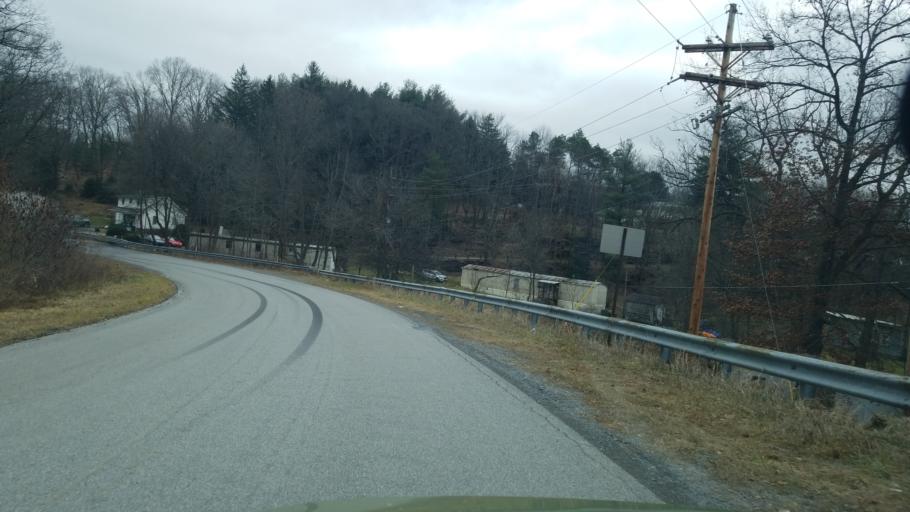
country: US
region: Pennsylvania
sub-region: Clearfield County
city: Clearfield
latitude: 41.0291
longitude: -78.4089
